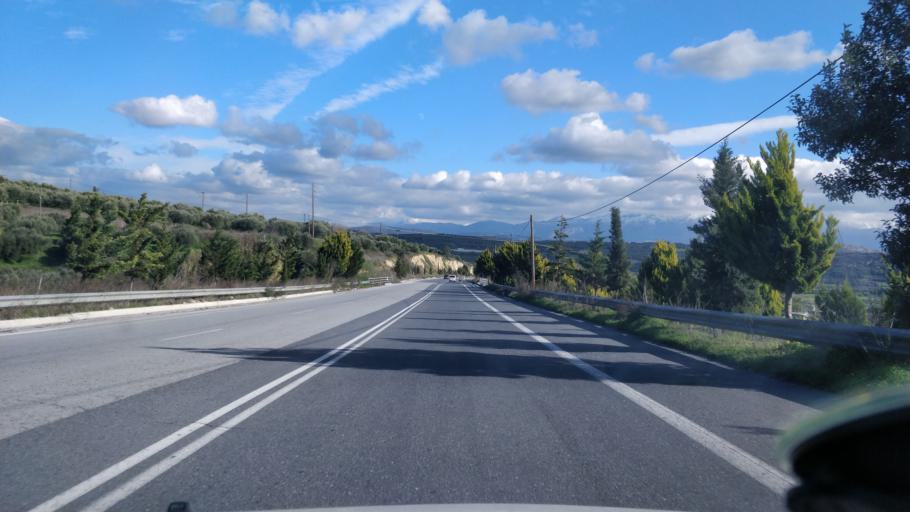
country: GR
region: Crete
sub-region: Nomos Irakleiou
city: Ano Arhanes
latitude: 35.2246
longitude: 25.1868
